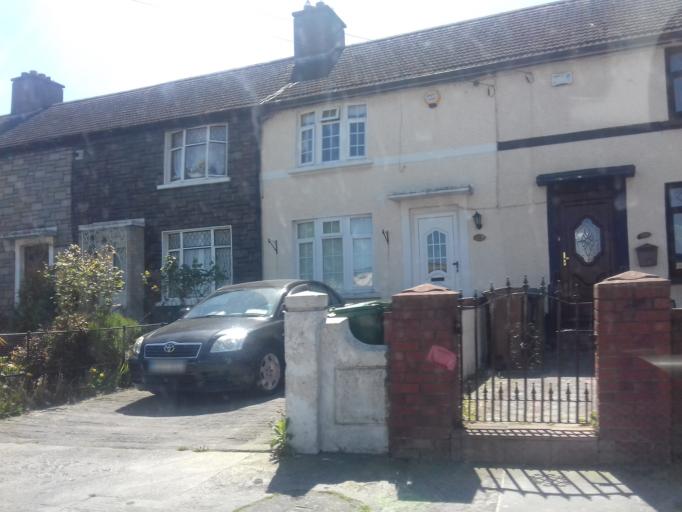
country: IE
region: Leinster
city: Cabra
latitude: 53.3702
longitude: -6.2916
